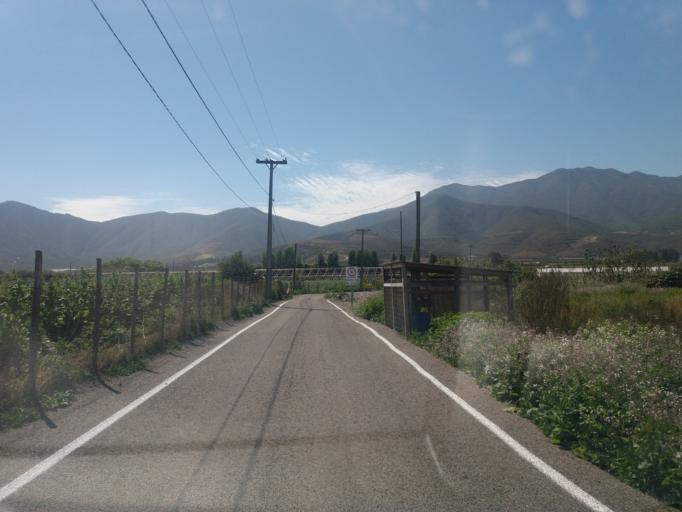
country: CL
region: Valparaiso
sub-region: Provincia de Quillota
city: Quillota
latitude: -32.8570
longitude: -71.2066
